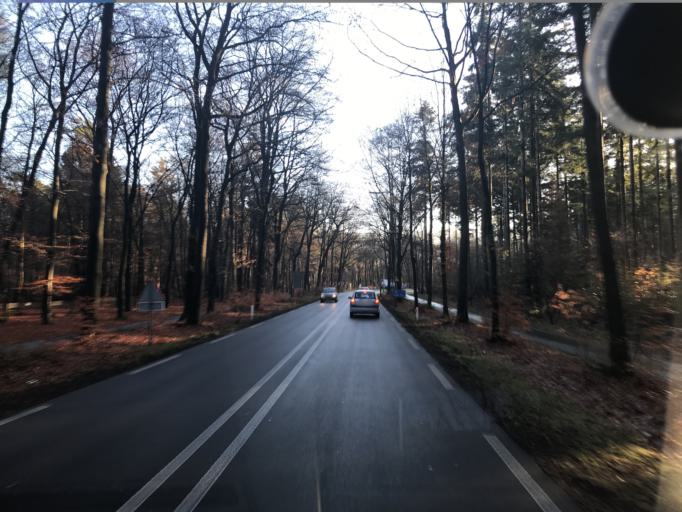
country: NL
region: Gelderland
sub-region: Gemeente Epe
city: Epe
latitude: 52.3613
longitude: 5.9254
